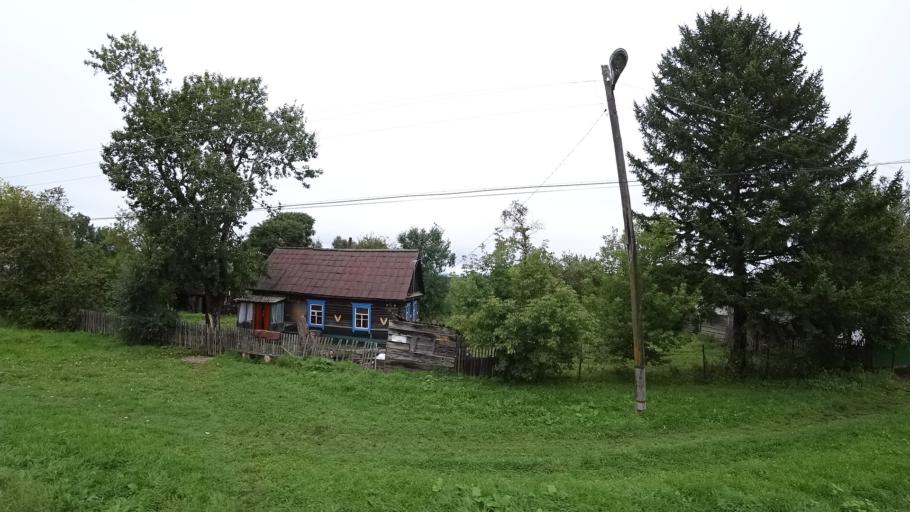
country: RU
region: Primorskiy
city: Monastyrishche
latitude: 44.0863
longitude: 132.5775
